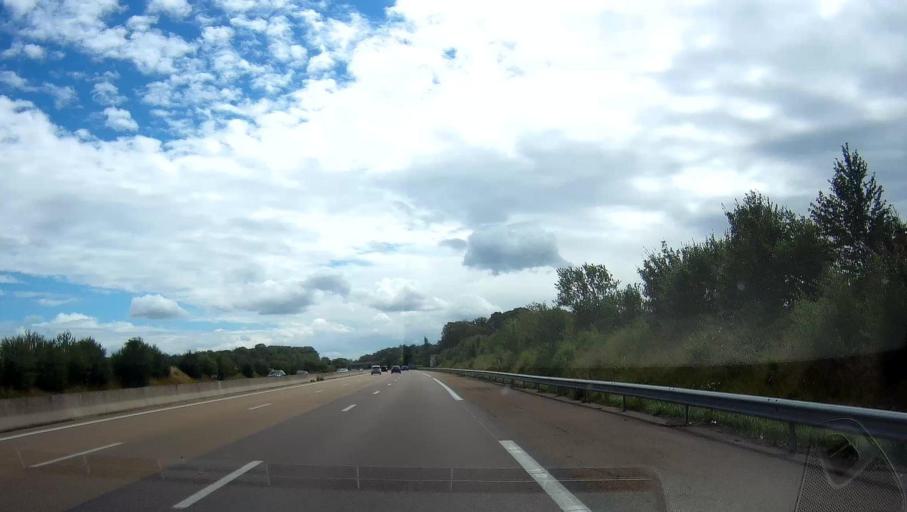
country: FR
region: Bourgogne
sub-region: Departement de la Cote-d'Or
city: Saint-Julien
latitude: 47.4351
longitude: 5.1670
